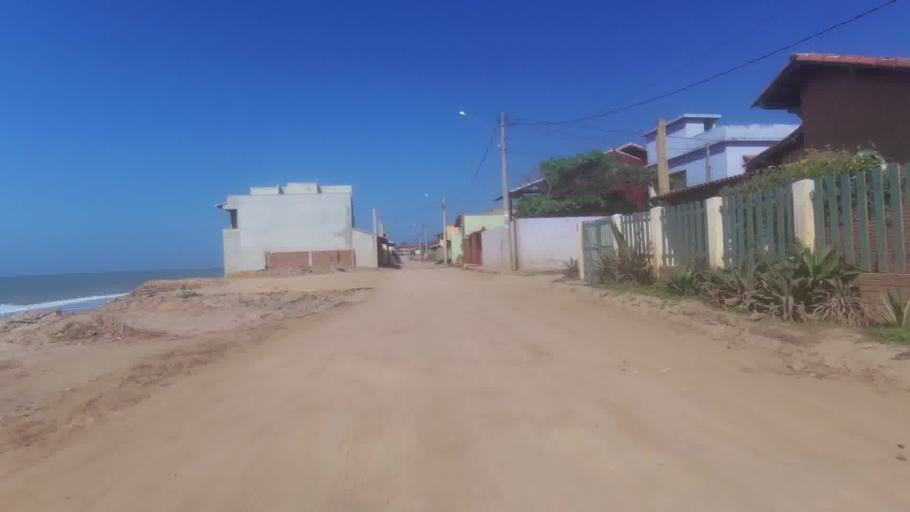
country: BR
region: Espirito Santo
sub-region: Marataizes
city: Marataizes
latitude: -21.0655
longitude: -40.8359
